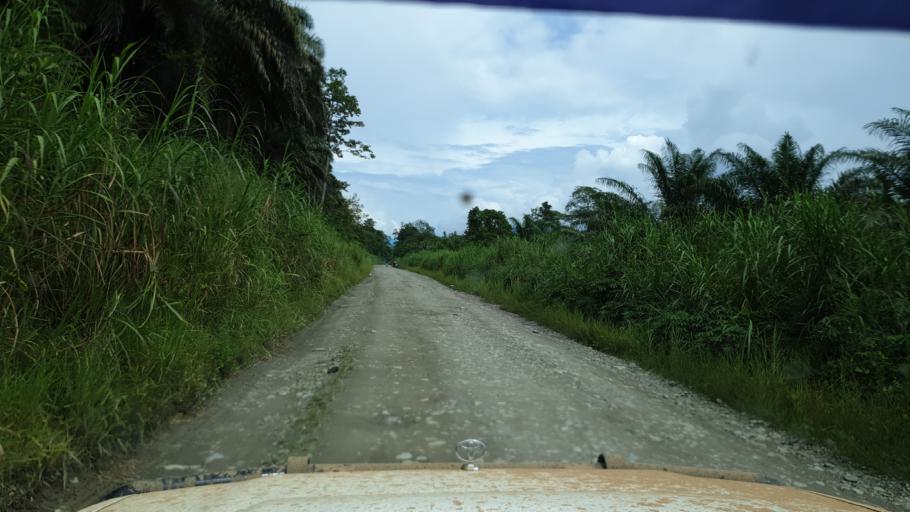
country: PG
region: Northern Province
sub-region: Sohe
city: Kokoda
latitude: -8.8921
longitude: 147.7486
